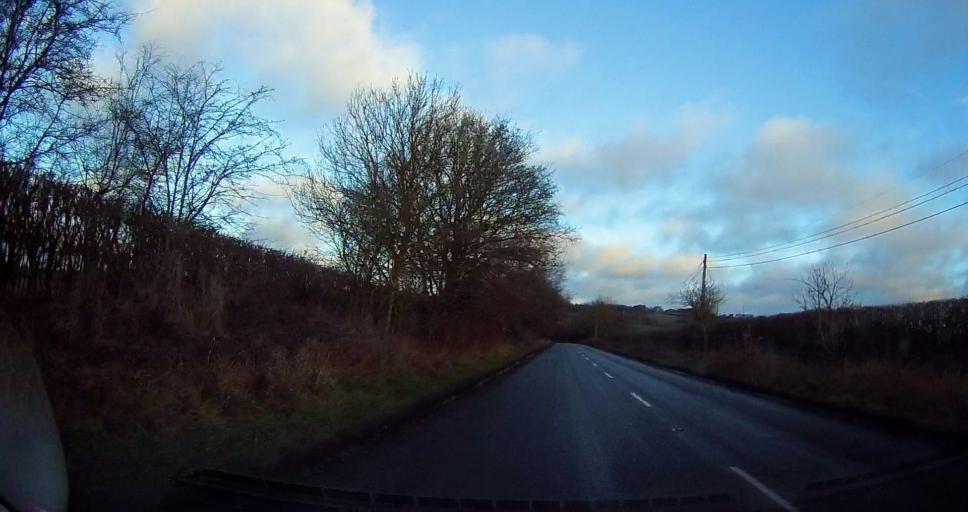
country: GB
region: England
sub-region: Kent
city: Westerham
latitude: 51.2723
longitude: 0.0862
